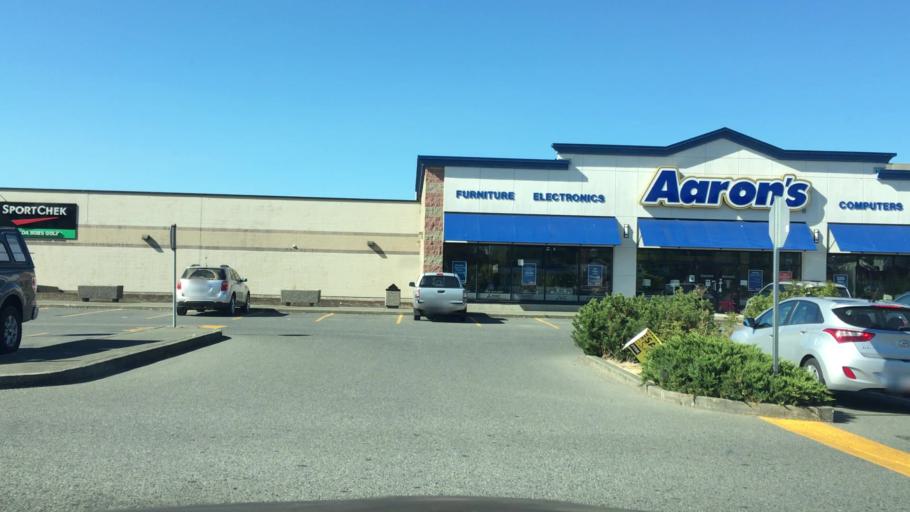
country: CA
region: British Columbia
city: Duncan
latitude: 48.7746
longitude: -123.7025
